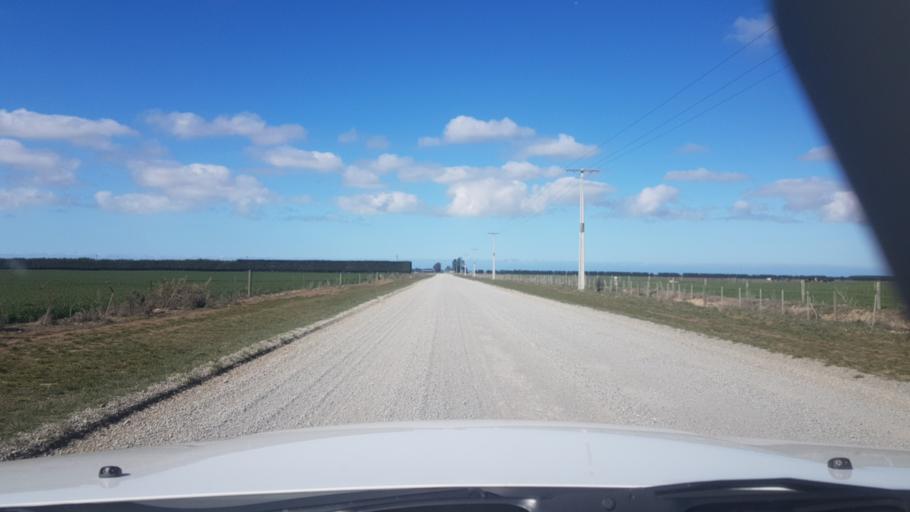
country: NZ
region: Canterbury
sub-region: Timaru District
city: Pleasant Point
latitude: -44.1235
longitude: 171.3976
